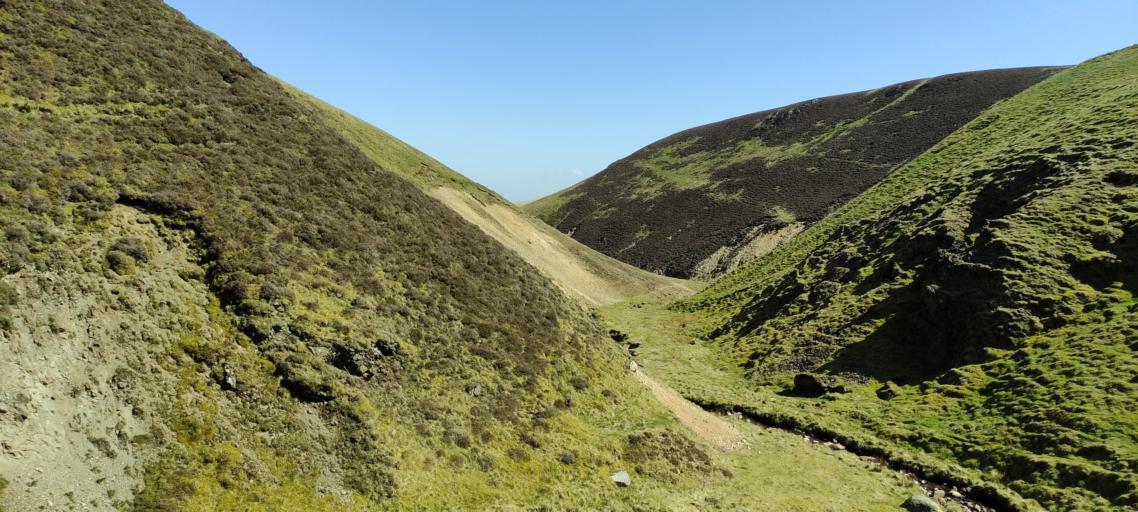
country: GB
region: England
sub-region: Cumbria
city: Keswick
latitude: 54.6942
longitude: -3.0878
